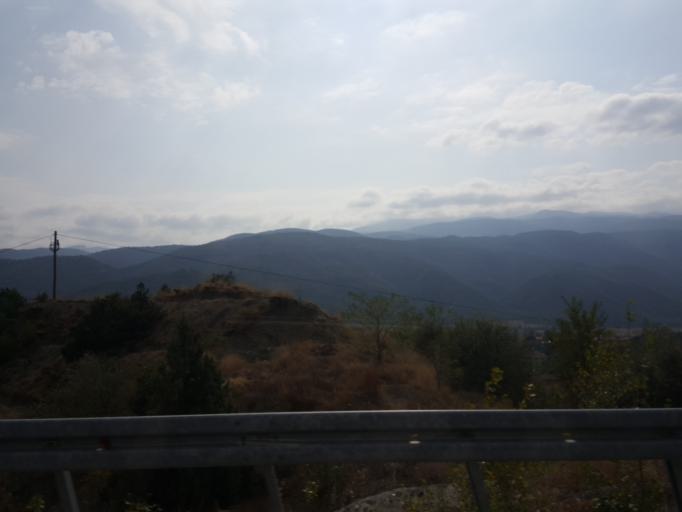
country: TR
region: Corum
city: Hacihamza
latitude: 41.1056
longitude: 34.3773
